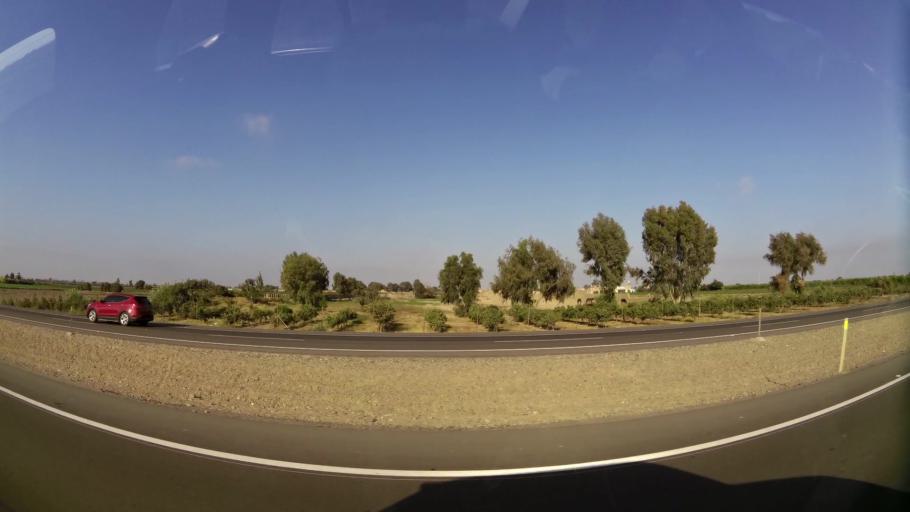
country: PE
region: Ica
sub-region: Provincia de Chincha
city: Chincha Baja
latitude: -13.4763
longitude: -76.1842
